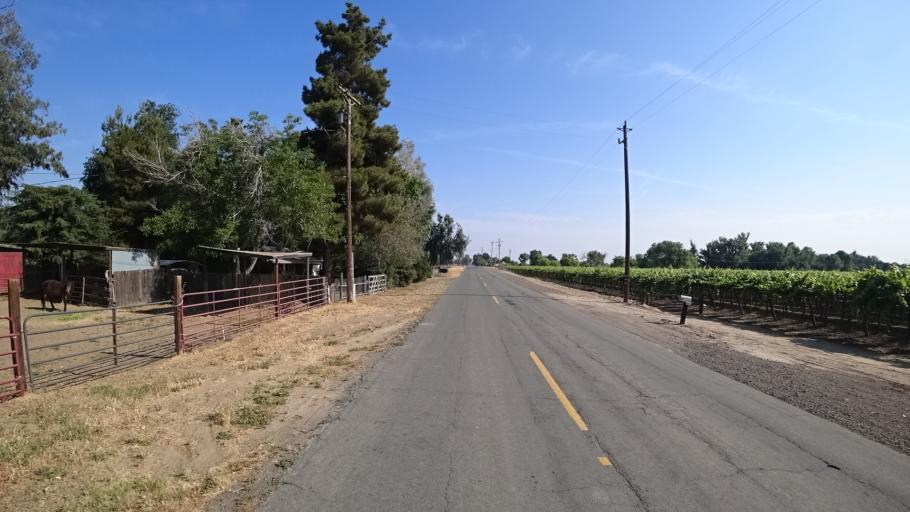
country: US
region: California
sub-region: Kings County
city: Lemoore
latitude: 36.3493
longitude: -119.8340
